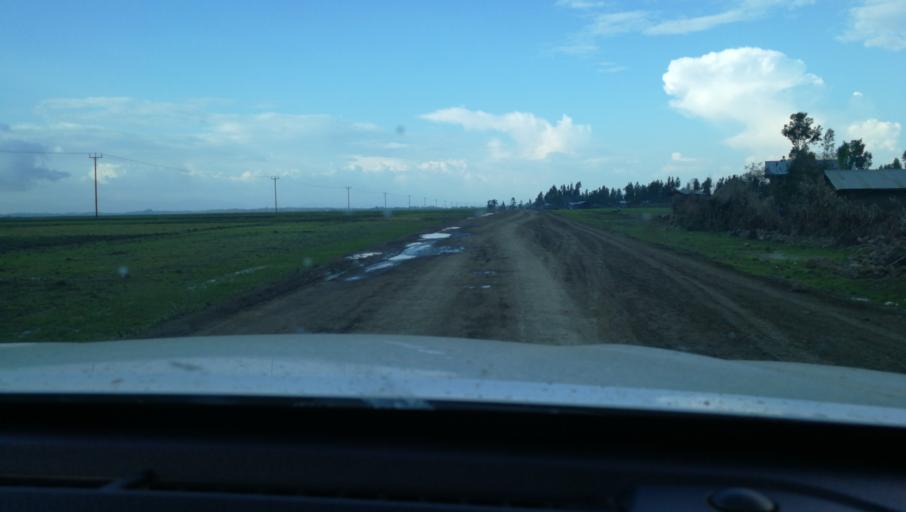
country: ET
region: Amhara
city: Were Ilu
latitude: 10.4428
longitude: 39.2569
